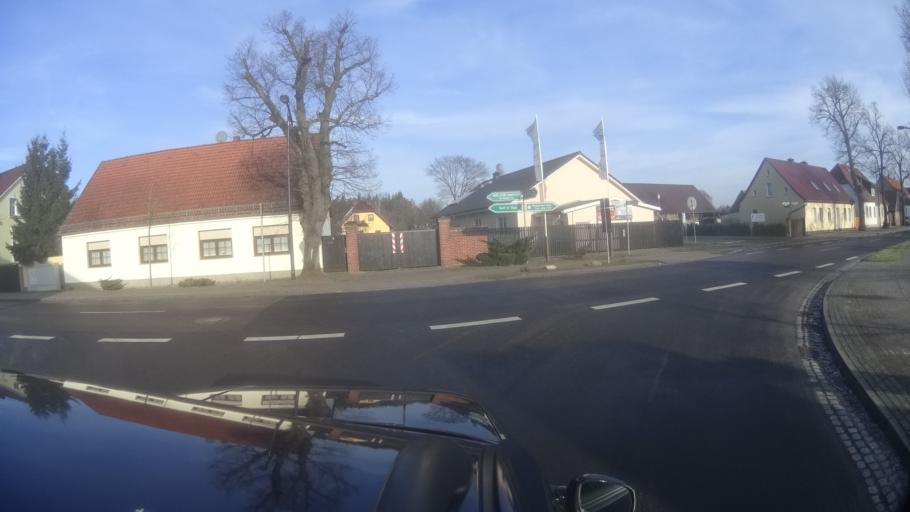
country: DE
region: Brandenburg
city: Kremmen
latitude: 52.8024
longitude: 13.0344
